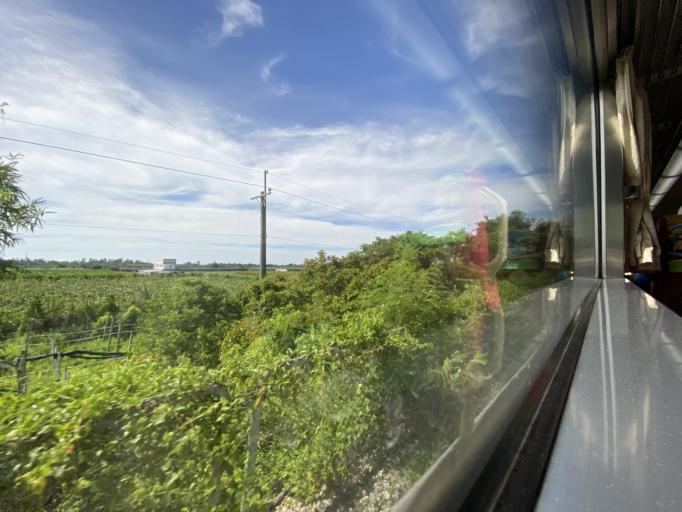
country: TW
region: Taiwan
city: Taitung City
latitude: 22.6821
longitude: 121.0444
